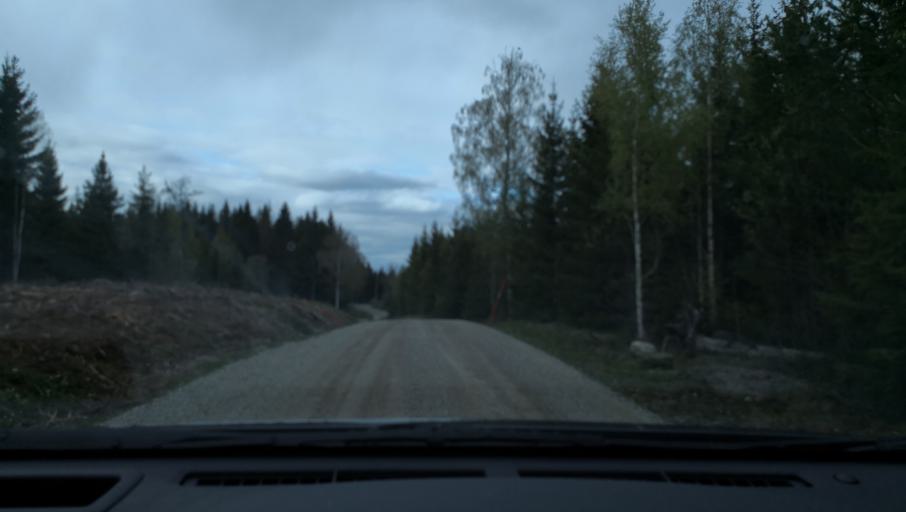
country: SE
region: Dalarna
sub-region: Saters Kommun
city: Saeter
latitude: 60.2058
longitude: 15.7450
